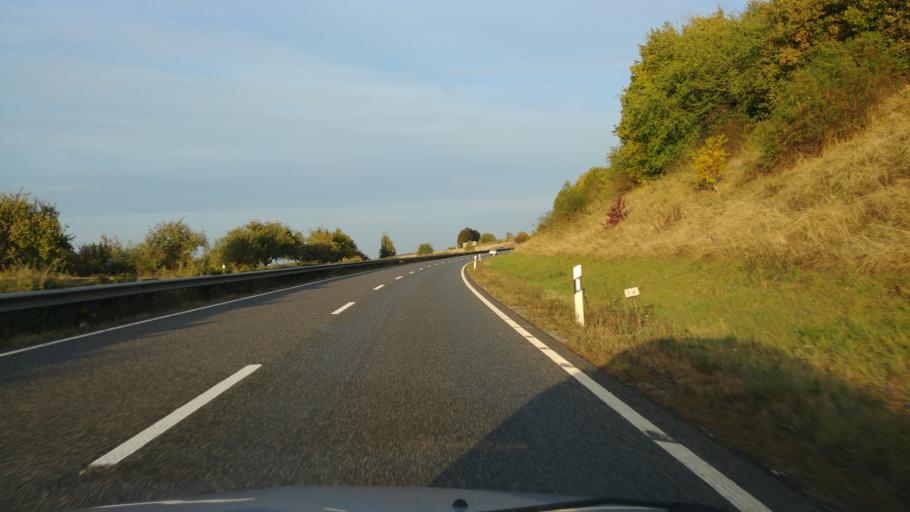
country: DE
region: Rheinland-Pfalz
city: Argenthal
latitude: 49.9771
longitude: 7.5901
